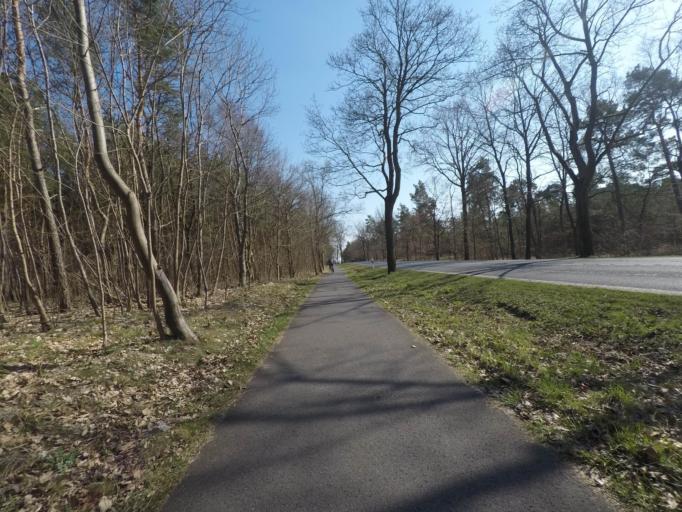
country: DE
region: Brandenburg
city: Britz
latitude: 52.8580
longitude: 13.7582
